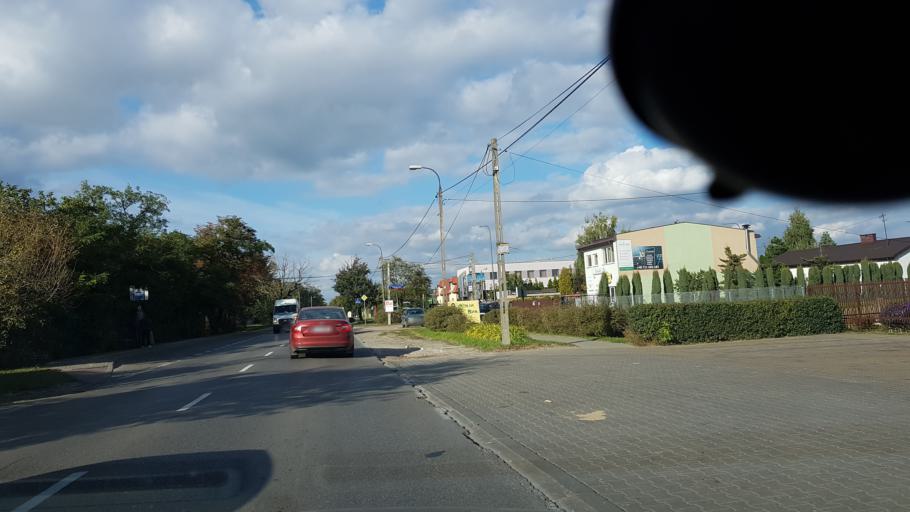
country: PL
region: Masovian Voivodeship
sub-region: Warszawa
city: Targowek
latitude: 52.3062
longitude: 21.0299
